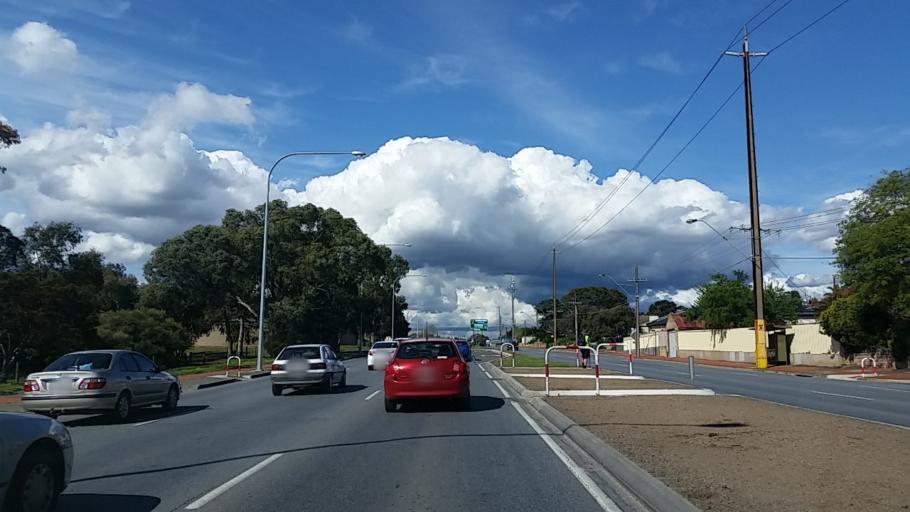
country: AU
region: South Australia
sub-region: Port Adelaide Enfield
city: Enfield
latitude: -34.8474
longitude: 138.6134
